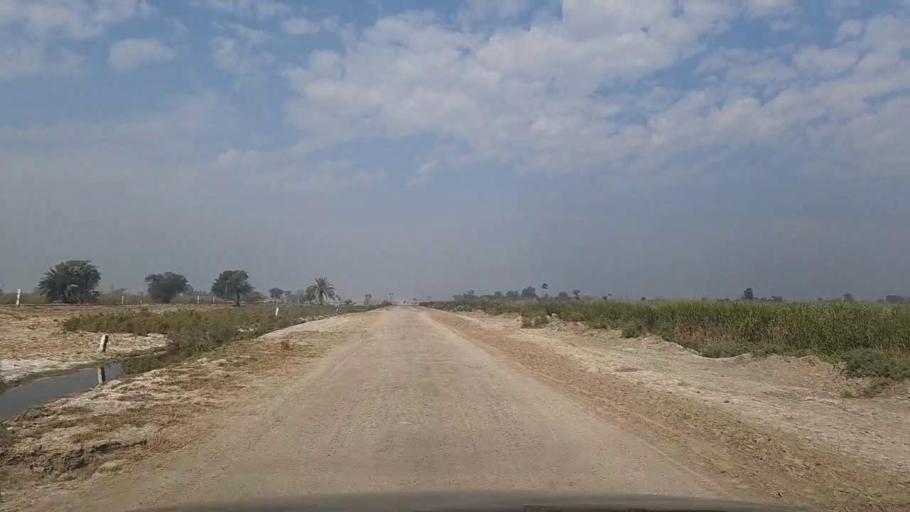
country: PK
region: Sindh
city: Daur
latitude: 26.3798
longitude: 68.3550
